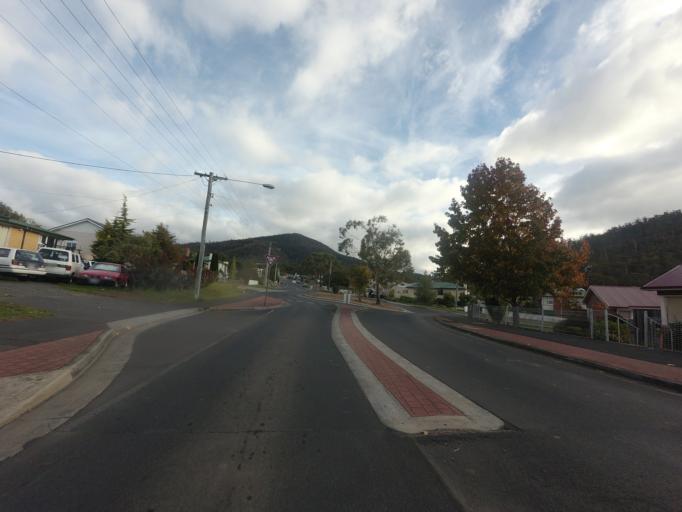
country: AU
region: Tasmania
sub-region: Glenorchy
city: Berriedale
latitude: -42.8096
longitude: 147.2435
